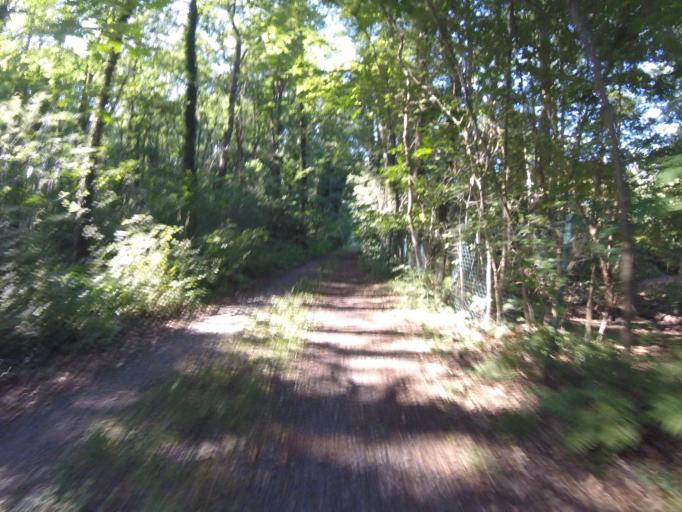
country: DE
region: Brandenburg
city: Wildau
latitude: 52.3202
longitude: 13.7140
